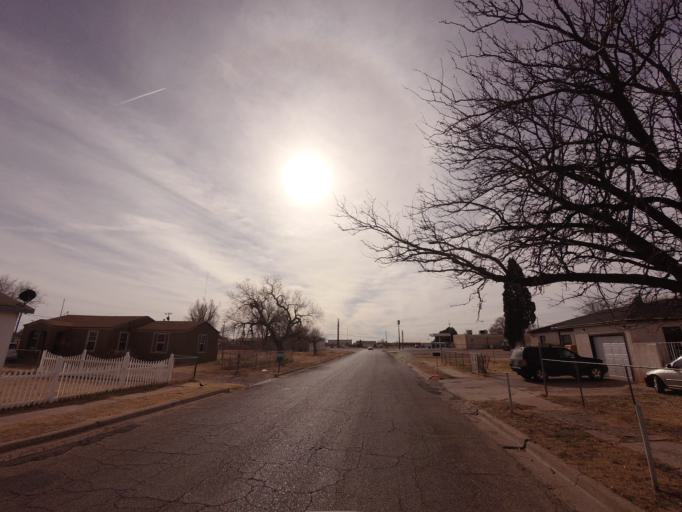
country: US
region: New Mexico
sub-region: Curry County
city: Clovis
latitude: 34.4058
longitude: -103.2375
